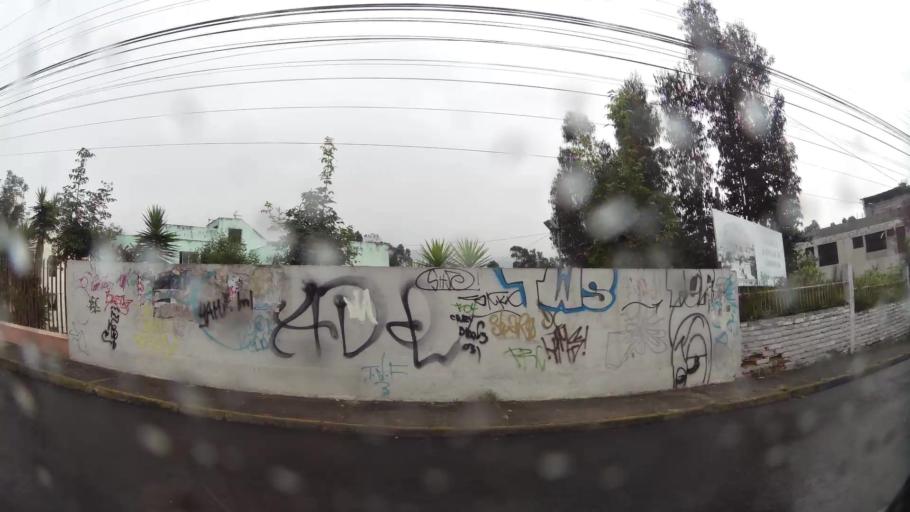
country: EC
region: Pichincha
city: Sangolqui
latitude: -0.2862
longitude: -78.4735
